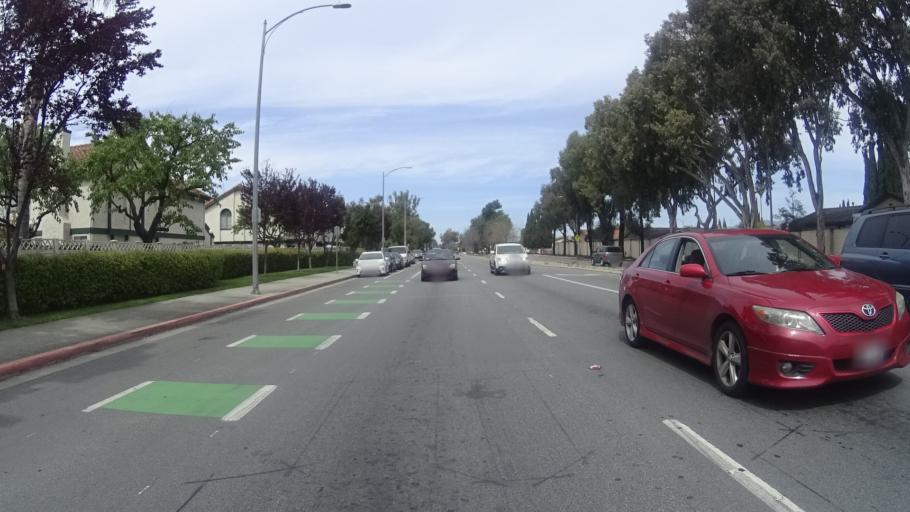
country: US
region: California
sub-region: Santa Clara County
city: Alum Rock
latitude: 37.3670
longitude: -121.8520
